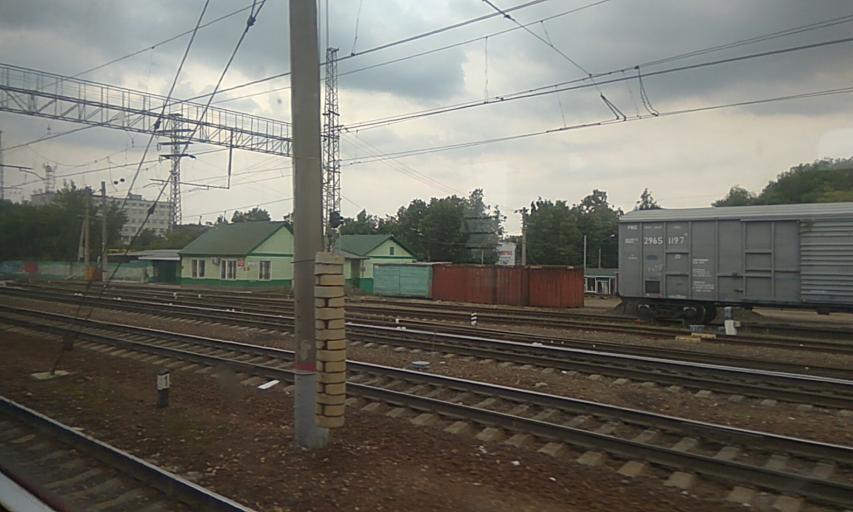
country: RU
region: Moskovskaya
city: Lyubertsy
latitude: 55.6797
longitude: 37.9017
